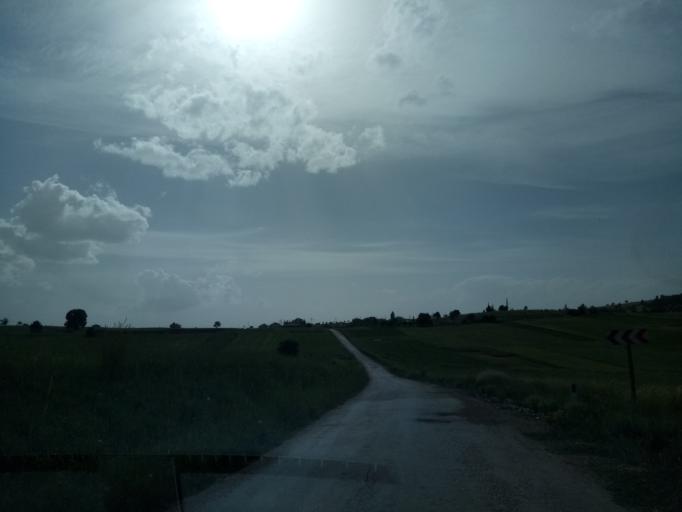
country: TR
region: Konya
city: Ahirli
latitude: 37.2837
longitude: 32.1874
